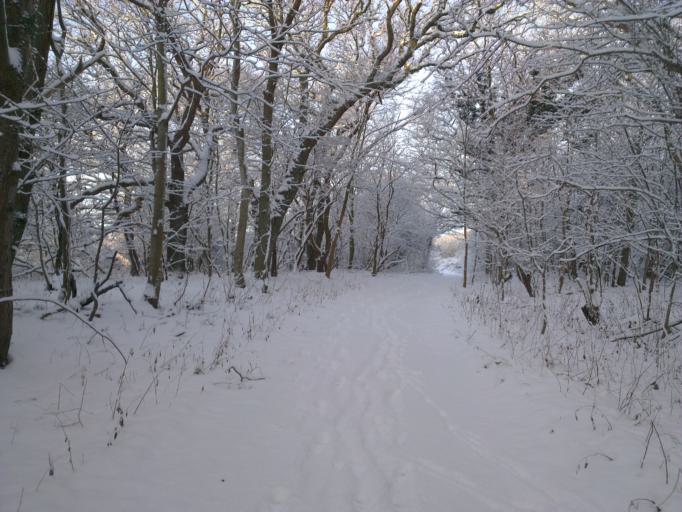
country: DK
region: Capital Region
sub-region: Frederikssund Kommune
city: Jaegerspris
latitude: 55.8547
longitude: 11.9594
